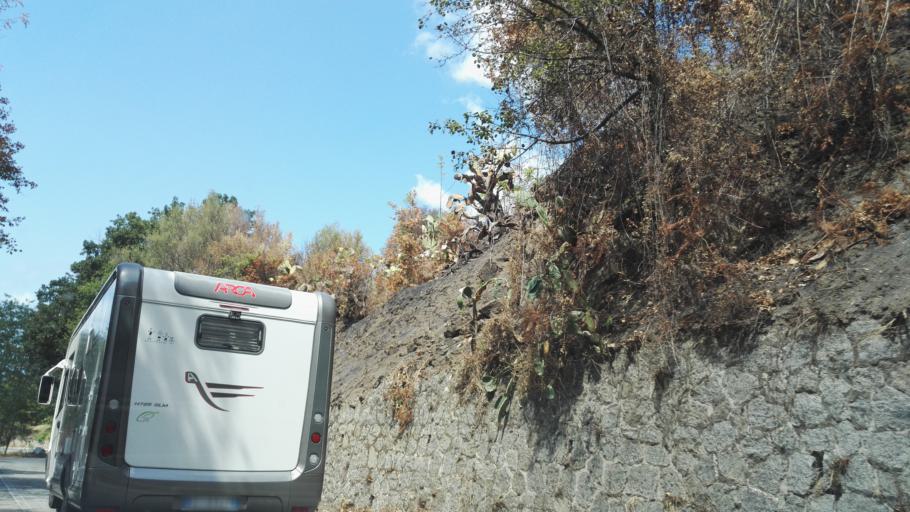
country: IT
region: Calabria
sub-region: Provincia di Vibo-Valentia
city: Joppolo
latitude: 38.5798
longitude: 15.9104
